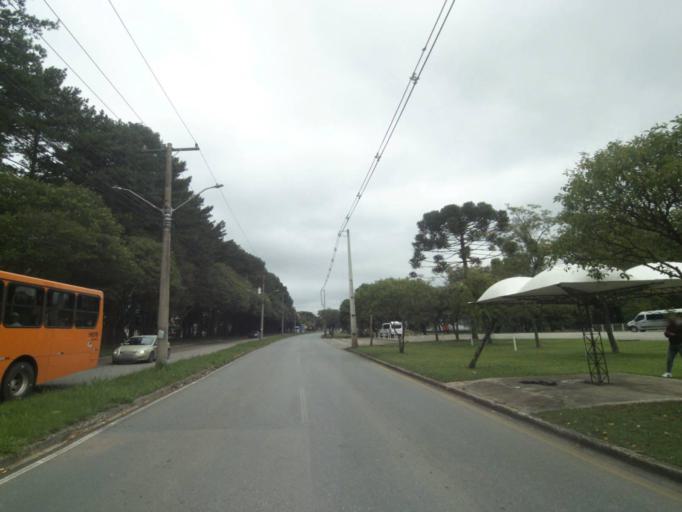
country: BR
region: Parana
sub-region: Araucaria
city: Araucaria
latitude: -25.5492
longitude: -49.3134
